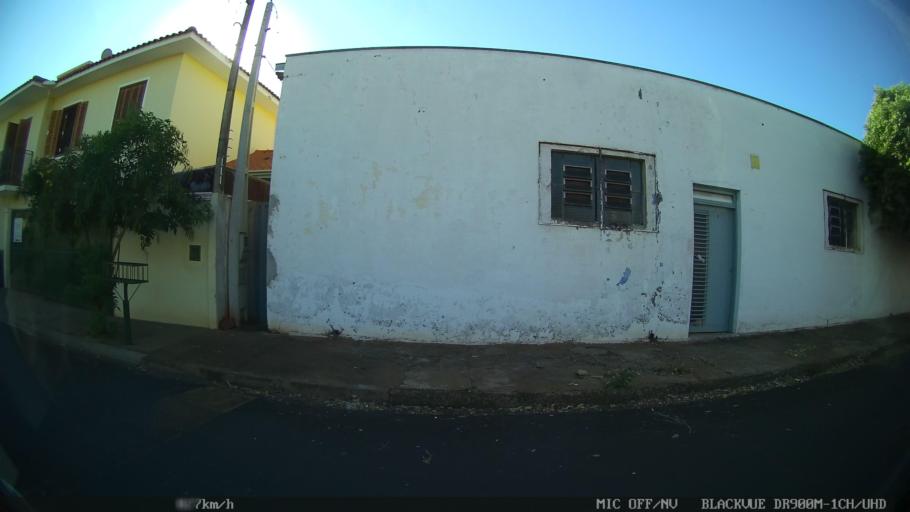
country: BR
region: Sao Paulo
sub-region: Olimpia
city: Olimpia
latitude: -20.7386
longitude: -48.9190
